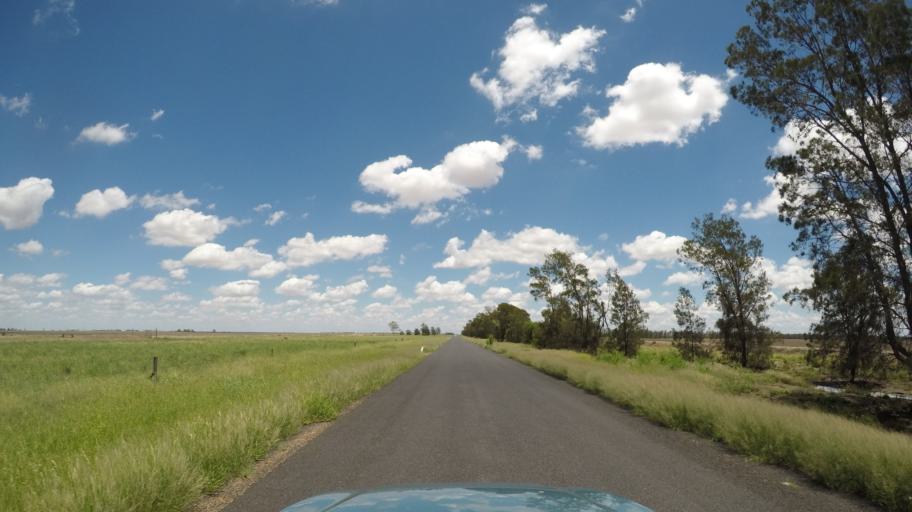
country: AU
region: Queensland
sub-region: Goondiwindi
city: Goondiwindi
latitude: -28.1763
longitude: 150.2593
